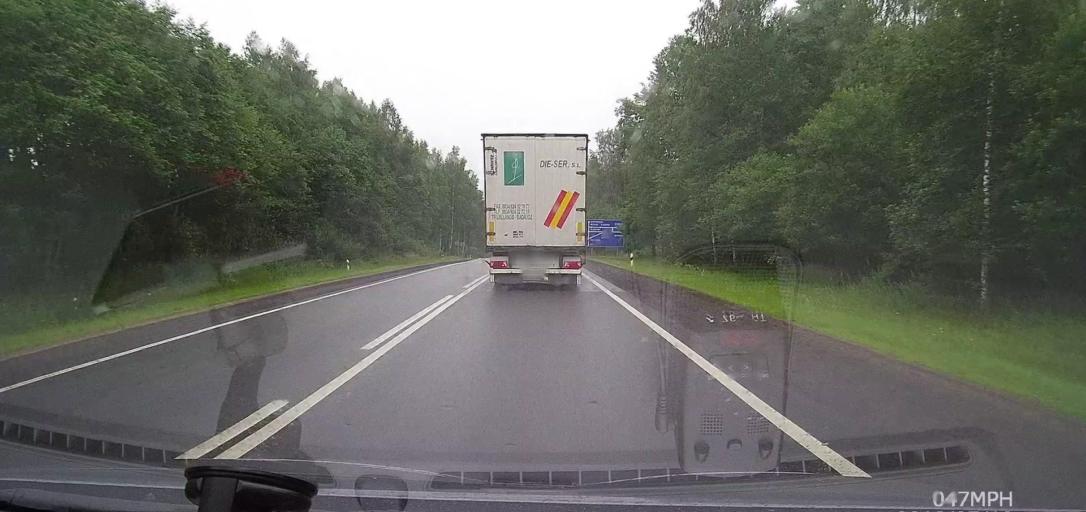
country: RU
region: Leningrad
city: Staraya Ladoga
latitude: 60.0353
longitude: 32.2263
